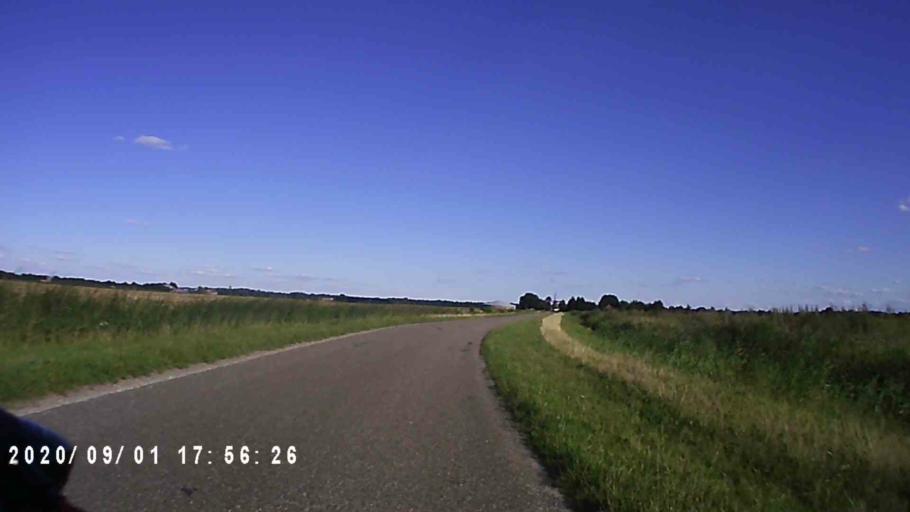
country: NL
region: Groningen
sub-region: Gemeente Slochteren
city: Slochteren
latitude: 53.2094
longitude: 6.7637
